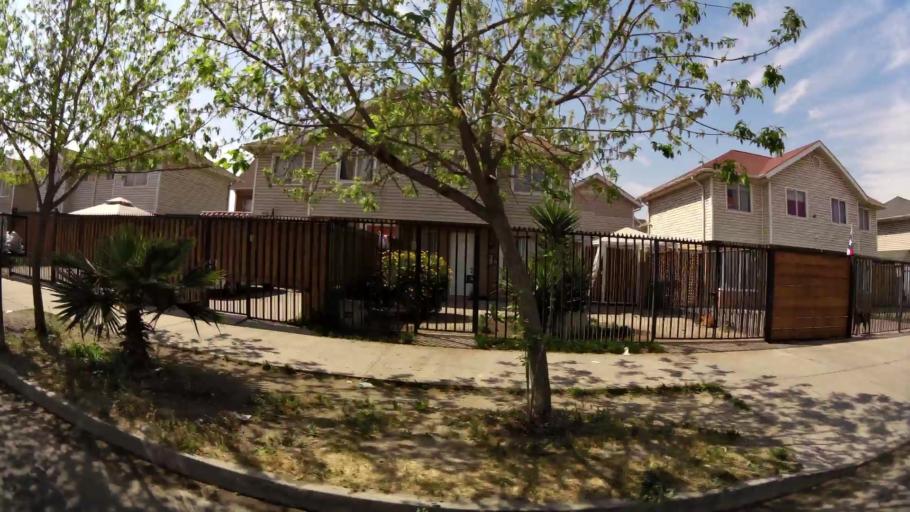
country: CL
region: Santiago Metropolitan
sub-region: Provincia de Cordillera
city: Puente Alto
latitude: -33.5939
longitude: -70.5953
